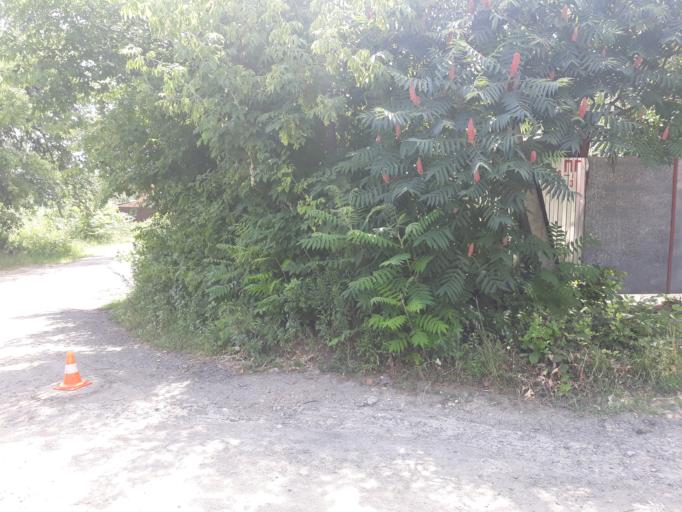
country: RU
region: Voronezj
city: Voronezh
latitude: 51.6913
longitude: 39.2312
